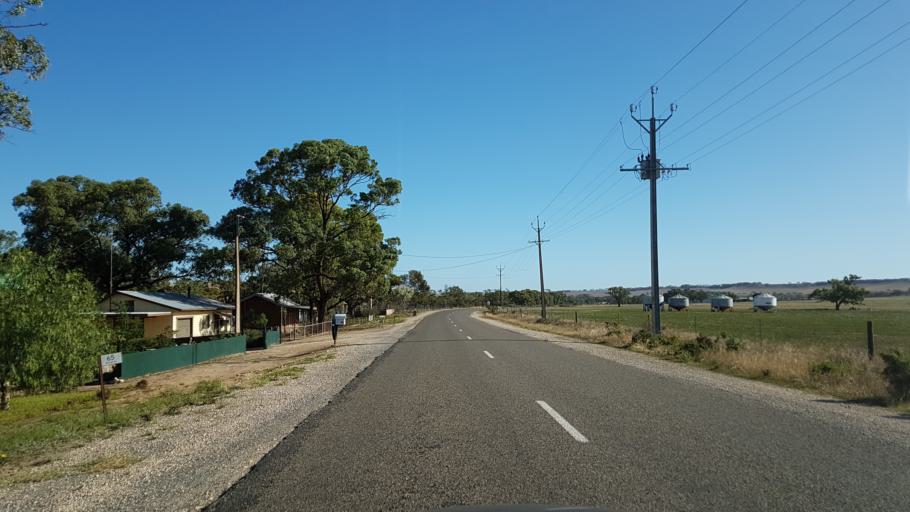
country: AU
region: South Australia
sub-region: Mid Murray
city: Mannum
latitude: -34.7687
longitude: 139.5661
